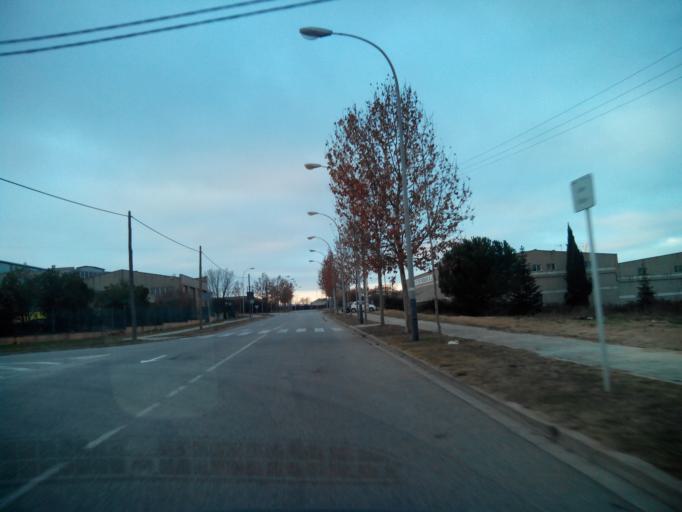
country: ES
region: Catalonia
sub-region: Provincia de Barcelona
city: Manresa
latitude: 41.7142
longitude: 1.8439
